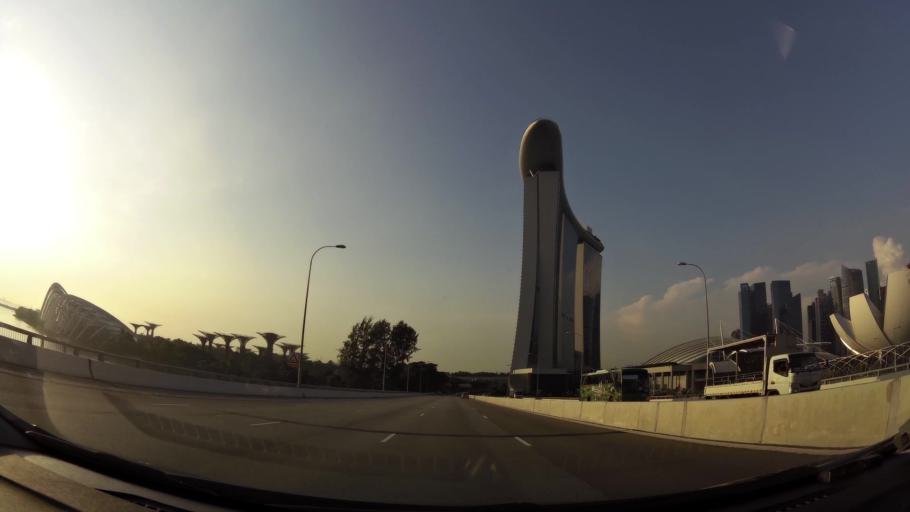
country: SG
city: Singapore
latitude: 1.2876
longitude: 103.8616
